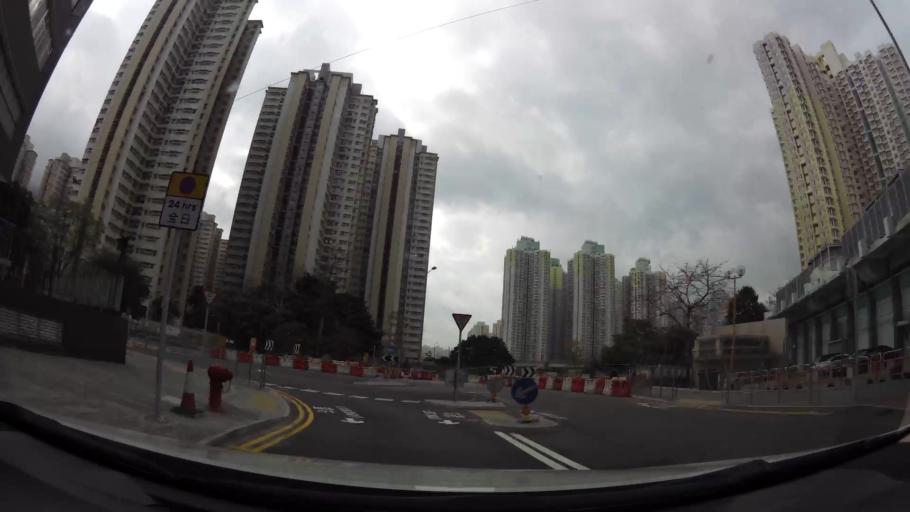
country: HK
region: Wong Tai Sin
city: Wong Tai Sin
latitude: 22.3365
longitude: 114.2007
